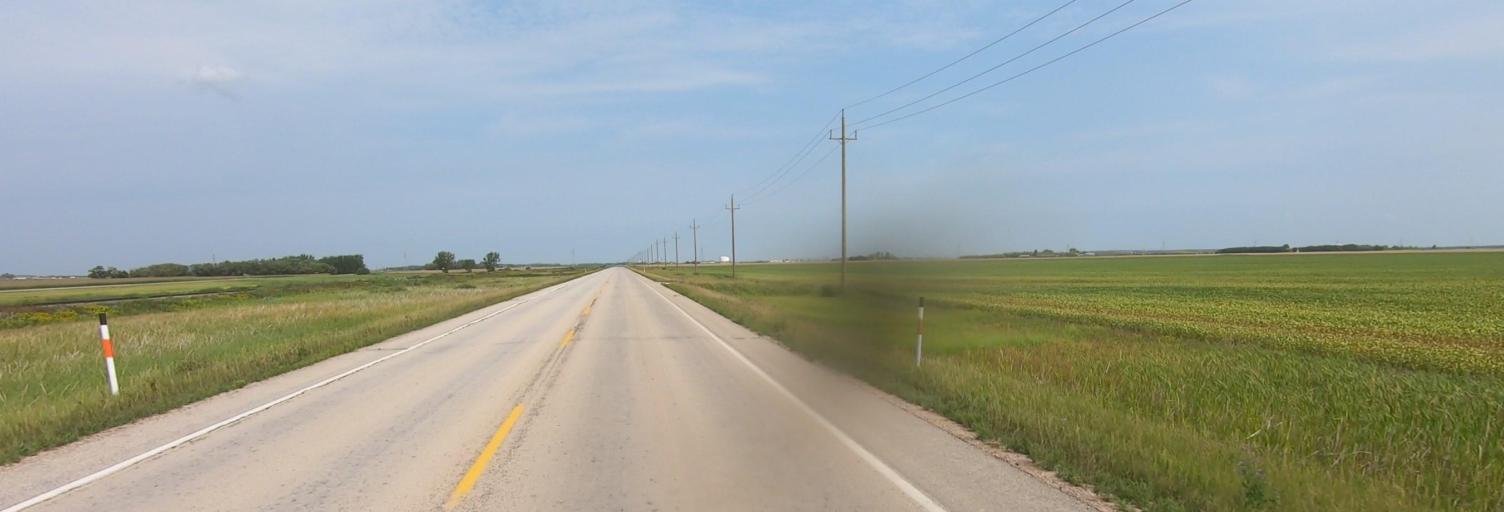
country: CA
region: Manitoba
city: Winnipeg
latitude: 49.7259
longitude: -97.2529
